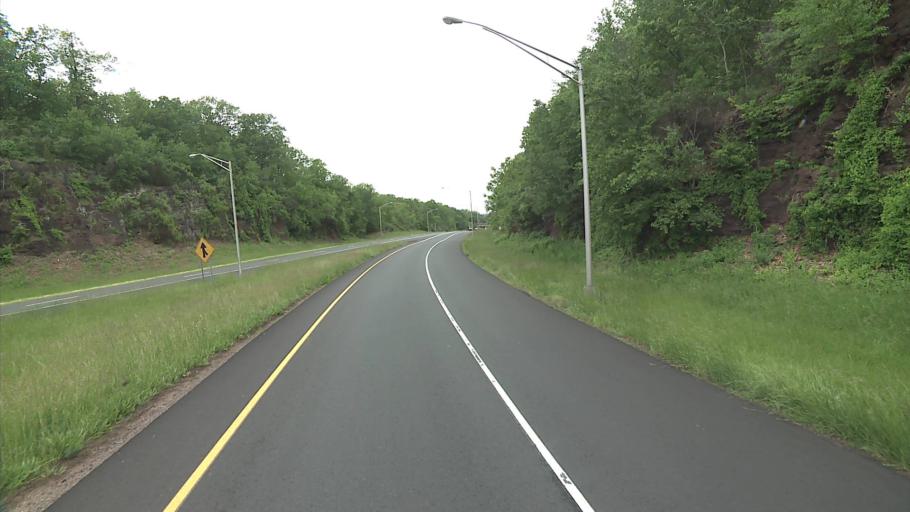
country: US
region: Connecticut
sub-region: Middlesex County
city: Cromwell
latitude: 41.6269
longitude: -72.6940
